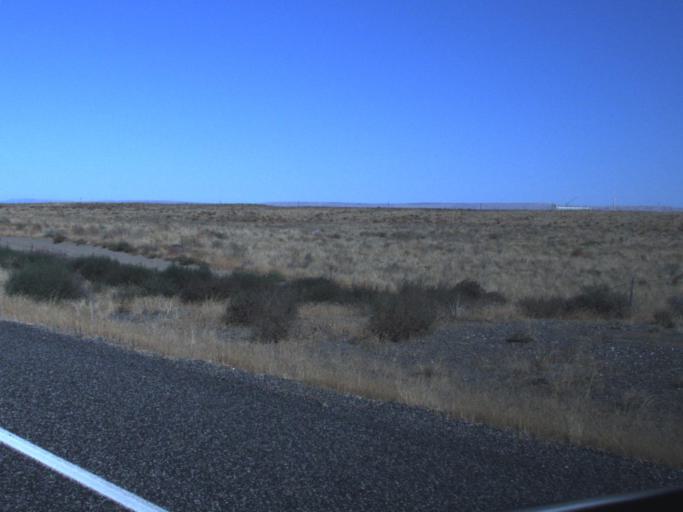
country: US
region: Washington
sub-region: Benton County
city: Benton City
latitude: 46.5028
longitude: -119.6174
